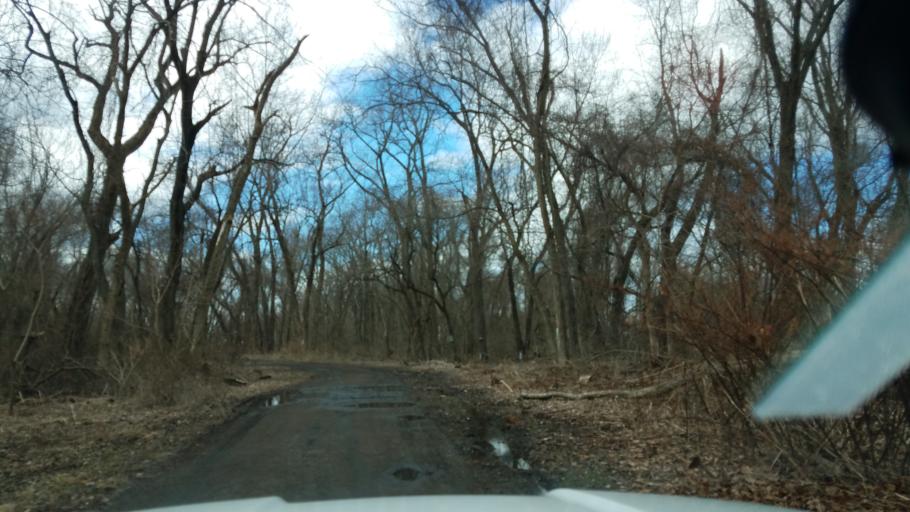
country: US
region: Connecticut
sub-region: Hartford County
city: Wethersfield
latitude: 41.7113
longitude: -72.6305
